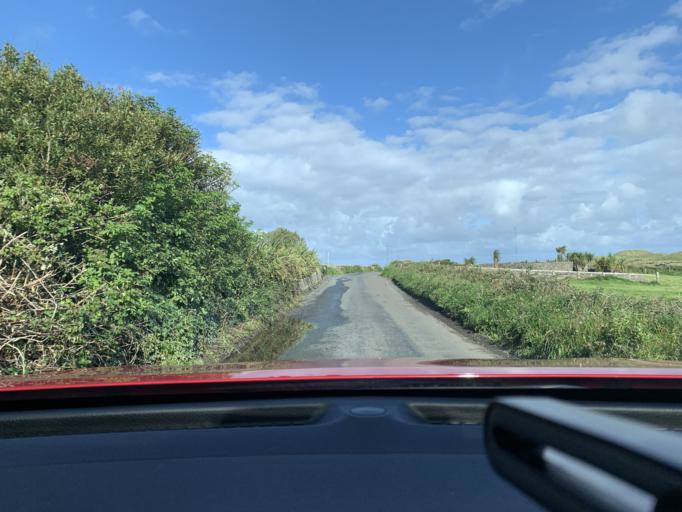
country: IE
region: Connaught
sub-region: Sligo
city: Strandhill
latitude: 54.3964
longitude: -8.5638
